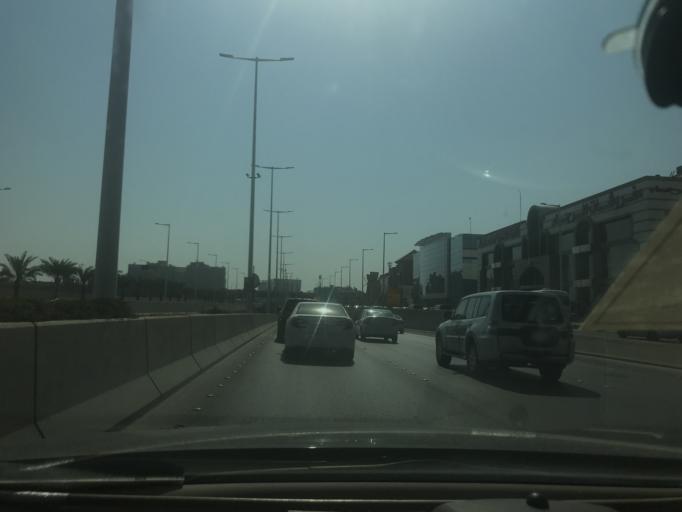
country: SA
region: Ar Riyad
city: Riyadh
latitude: 24.6971
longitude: 46.7230
